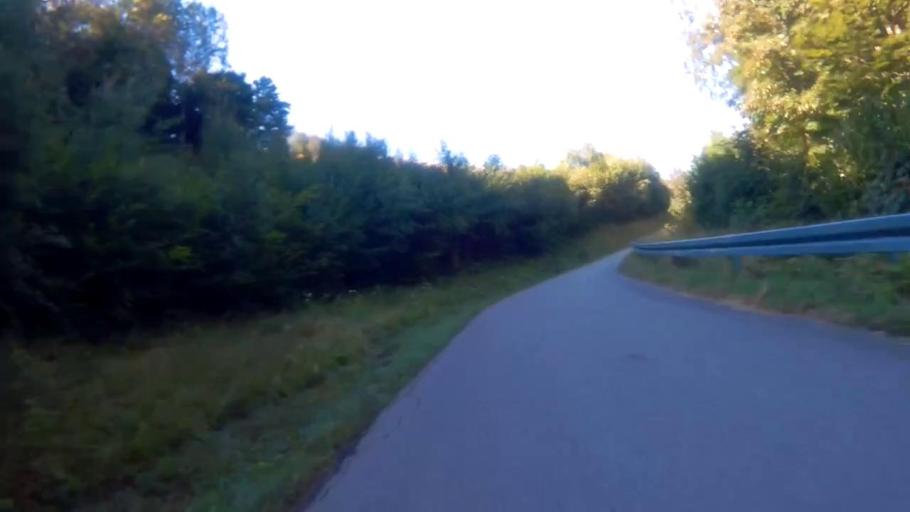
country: DE
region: Baden-Wuerttemberg
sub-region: Freiburg Region
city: Tunau
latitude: 47.7594
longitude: 7.9187
